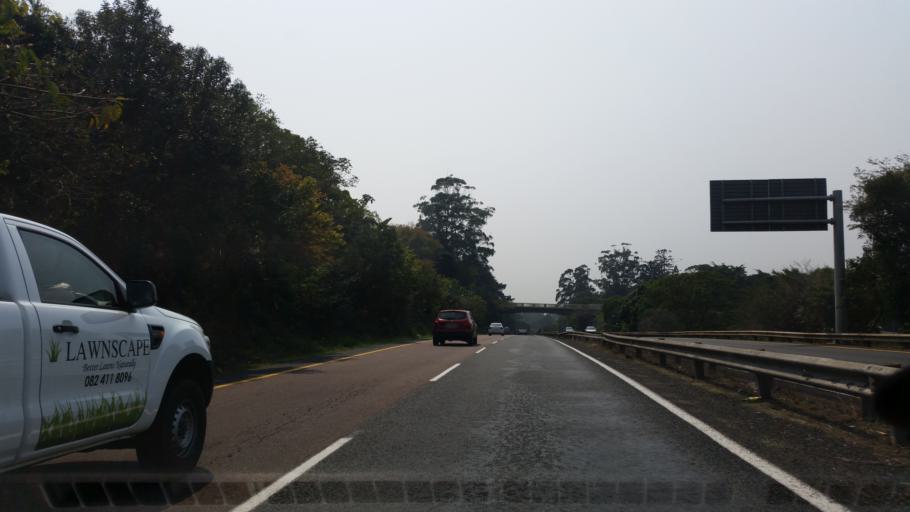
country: ZA
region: KwaZulu-Natal
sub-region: eThekwini Metropolitan Municipality
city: Berea
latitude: -29.8340
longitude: 30.9206
